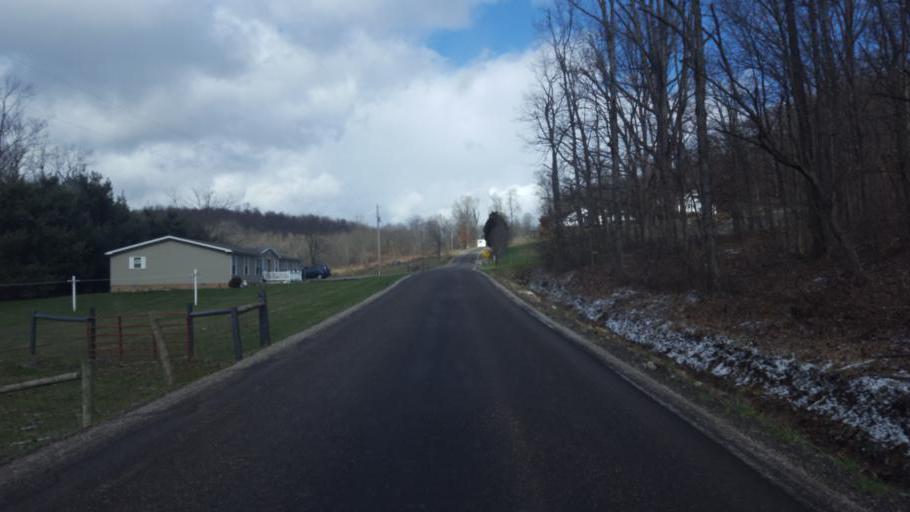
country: US
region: Ohio
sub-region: Tuscarawas County
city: Sugarcreek
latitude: 40.4275
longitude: -81.7720
